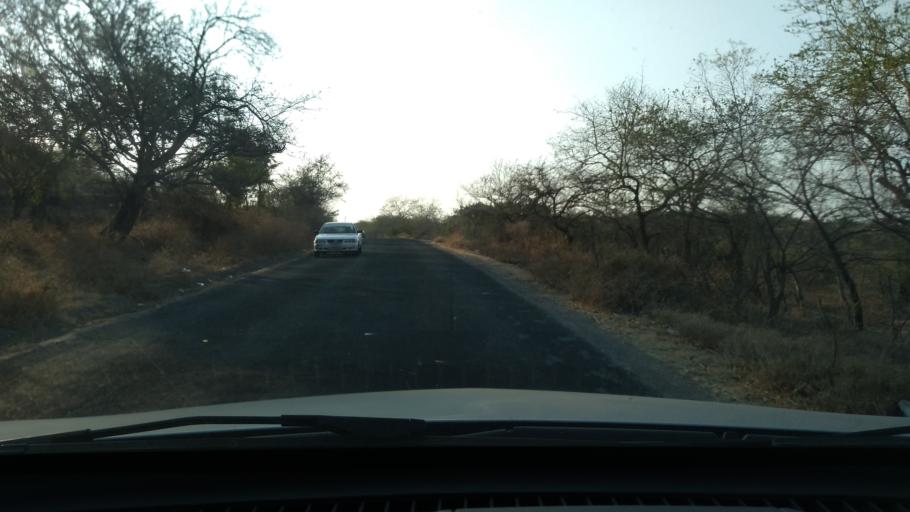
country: MX
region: Morelos
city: Puente de Ixtla
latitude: 18.6005
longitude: -99.3083
